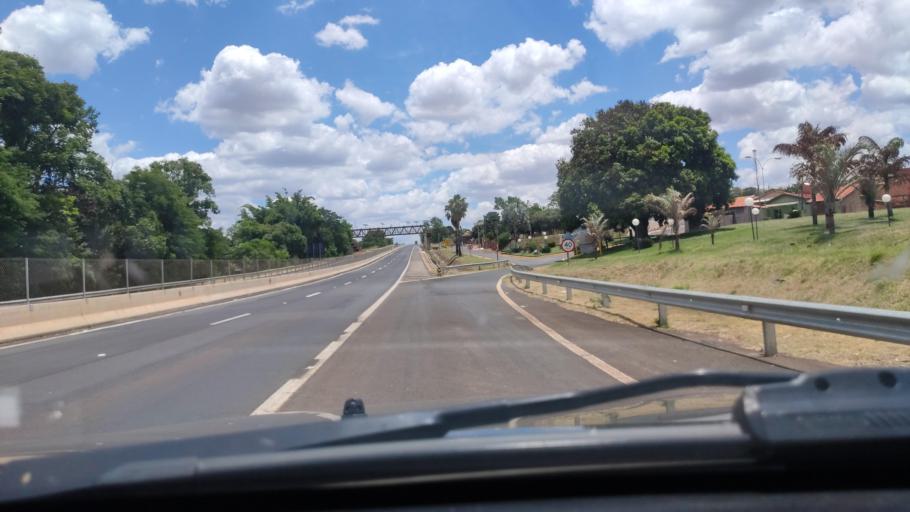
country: BR
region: Sao Paulo
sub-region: Duartina
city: Duartina
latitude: -22.6965
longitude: -49.4281
